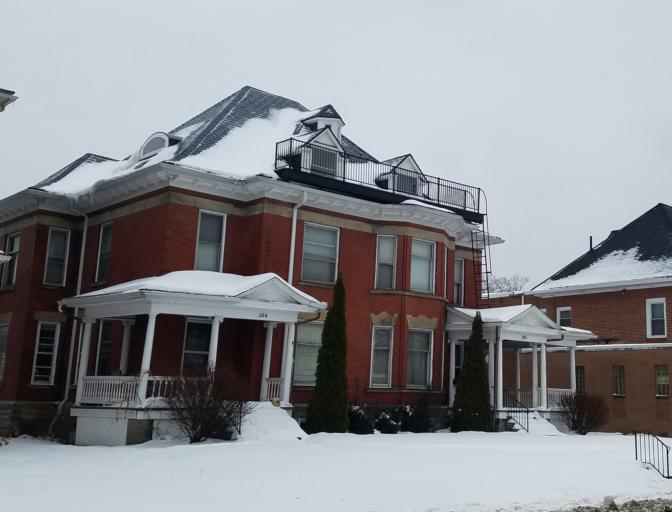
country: US
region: Pennsylvania
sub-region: Mercer County
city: Greenville
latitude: 41.4066
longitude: -80.3846
